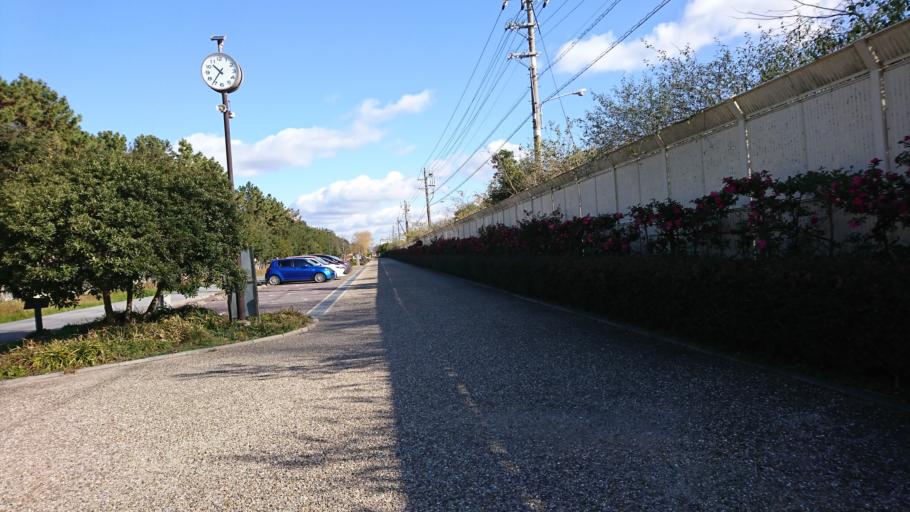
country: JP
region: Hyogo
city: Kakogawacho-honmachi
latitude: 34.7464
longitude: 134.7782
